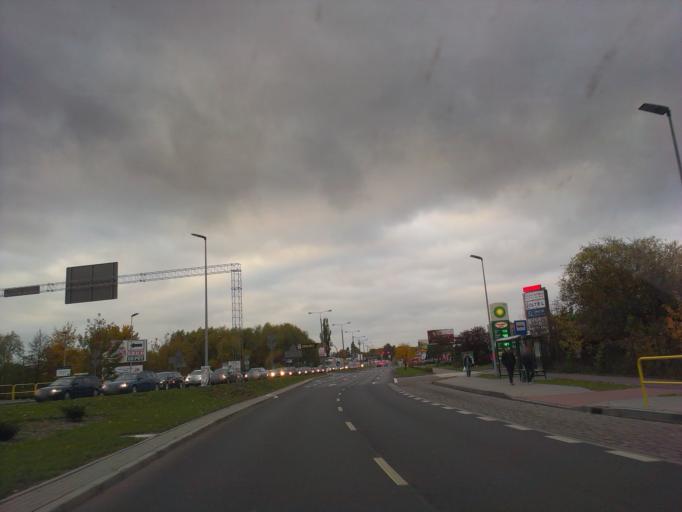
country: PL
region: Kujawsko-Pomorskie
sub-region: Torun
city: Torun
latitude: 53.0278
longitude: 18.6112
